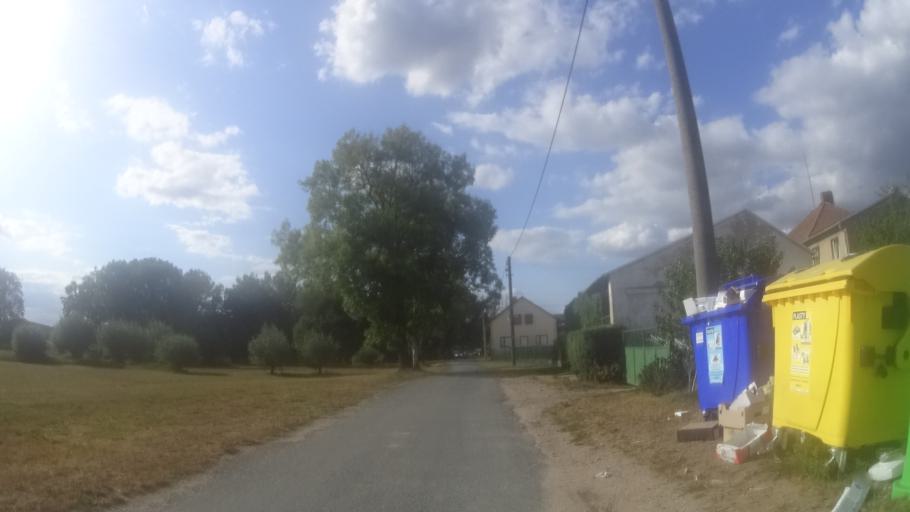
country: CZ
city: Albrechtice nad Orlici
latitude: 50.1669
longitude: 16.0317
